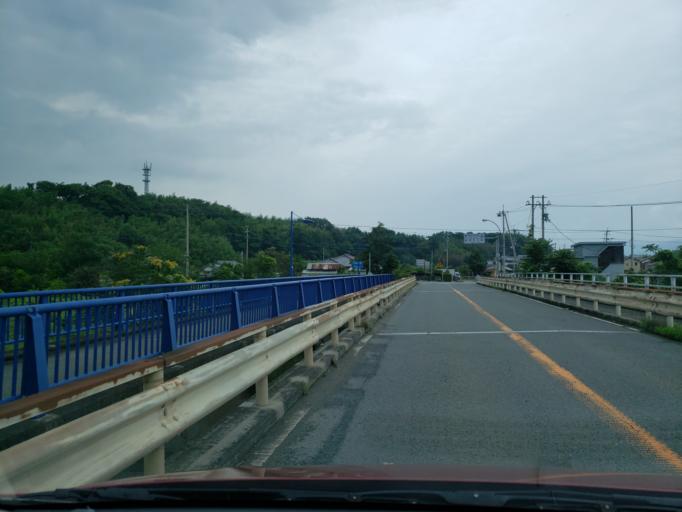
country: JP
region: Tokushima
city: Kamojimacho-jogejima
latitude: 34.1026
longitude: 134.2765
